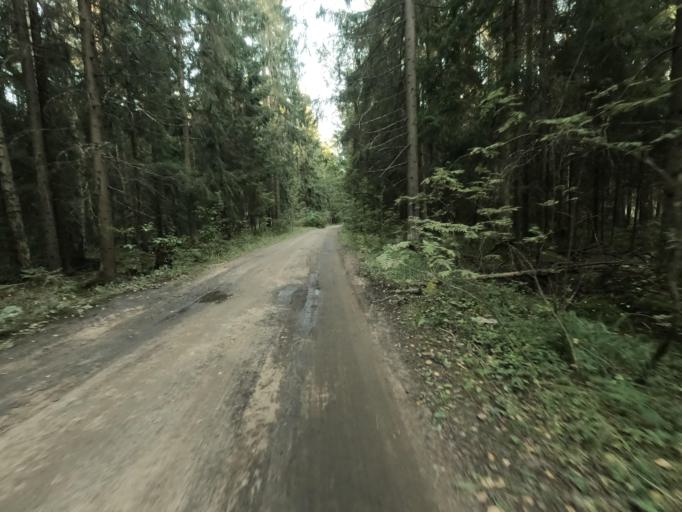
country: RU
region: Leningrad
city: Otradnoye
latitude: 59.8274
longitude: 30.7716
